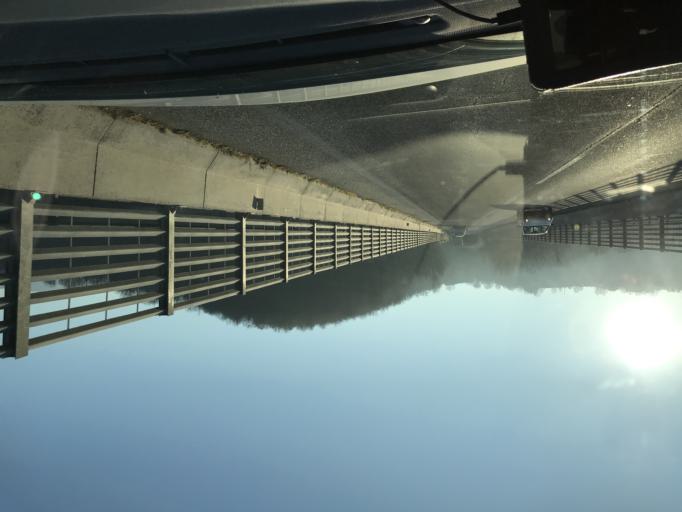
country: IT
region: Latium
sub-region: Provincia di Rieti
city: Pescorocchiano
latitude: 42.2432
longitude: 13.1700
